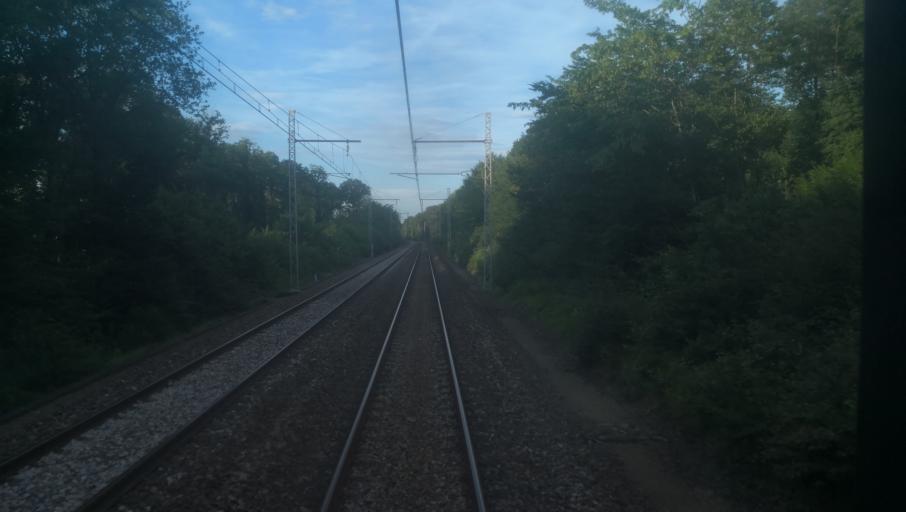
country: FR
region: Centre
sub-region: Departement de l'Indre
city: Saint-Marcel
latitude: 46.6644
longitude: 1.5353
